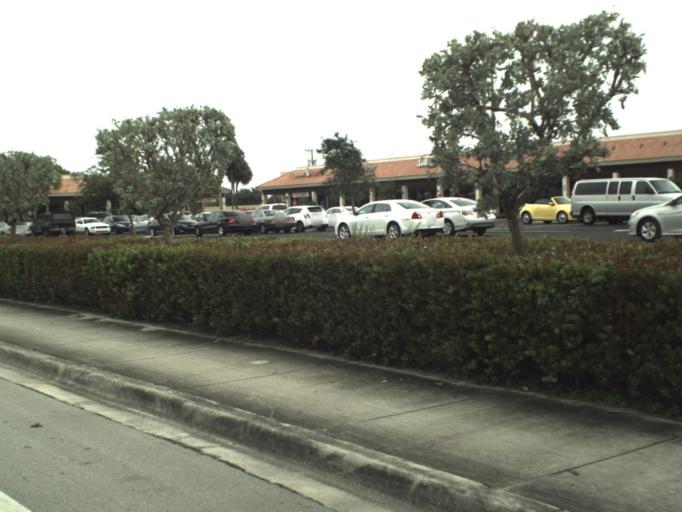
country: US
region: Florida
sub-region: Palm Beach County
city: Haverhill
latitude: 26.6896
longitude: -80.1116
